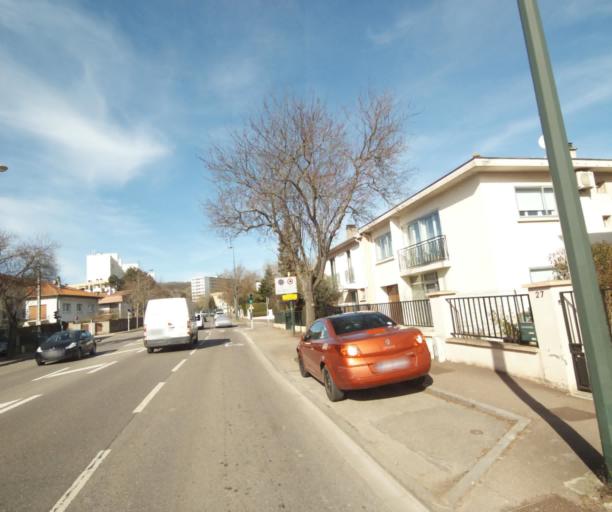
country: FR
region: Lorraine
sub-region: Departement de Meurthe-et-Moselle
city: Villers-les-Nancy
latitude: 48.6766
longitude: 6.1478
